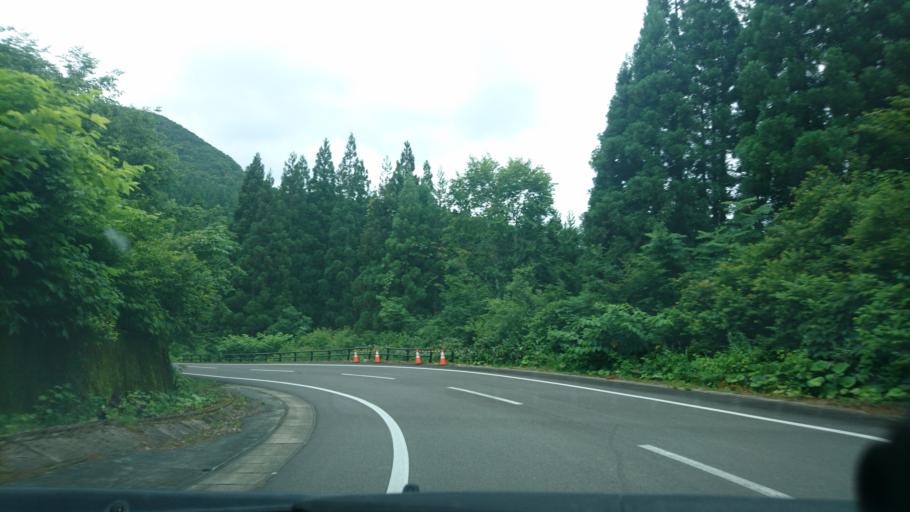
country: JP
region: Akita
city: Yuzawa
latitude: 39.1621
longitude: 140.7503
